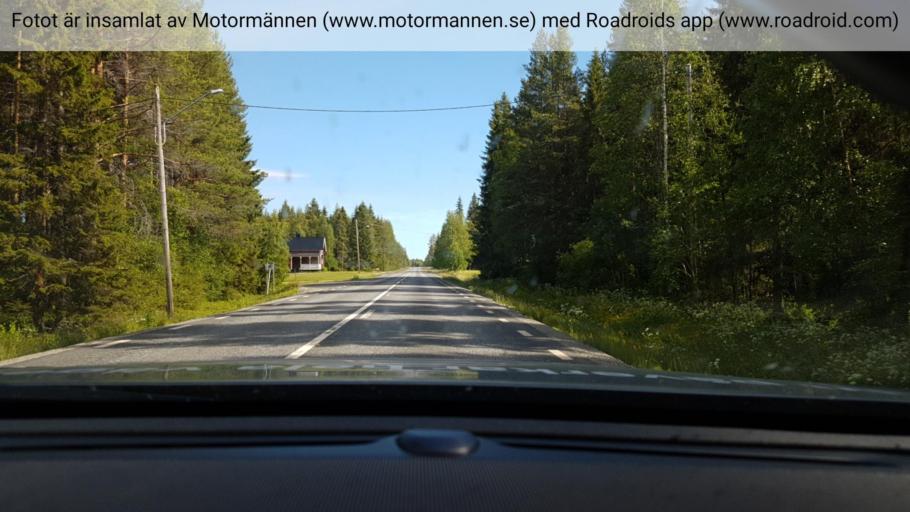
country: SE
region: Vaesterbotten
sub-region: Lycksele Kommun
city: Soderfors
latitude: 64.8101
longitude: 18.0779
